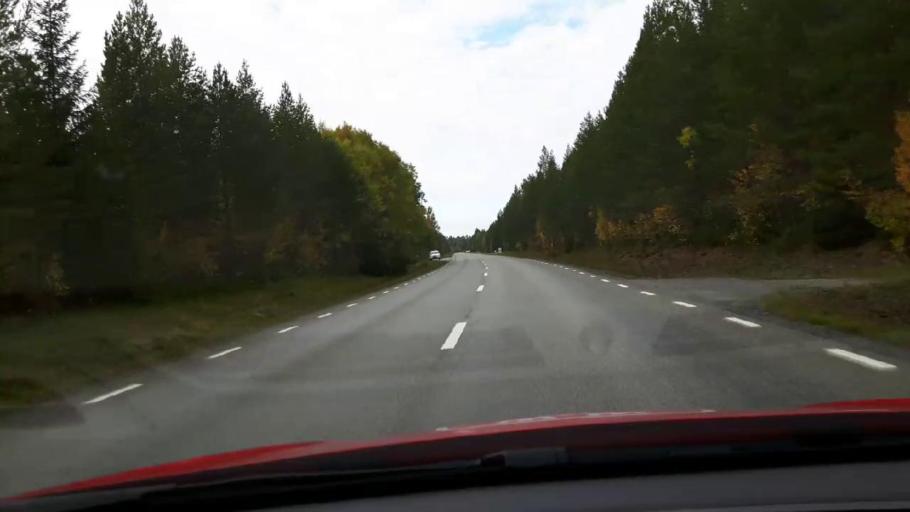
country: SE
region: Jaemtland
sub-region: Krokoms Kommun
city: Valla
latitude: 63.2566
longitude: 13.9907
